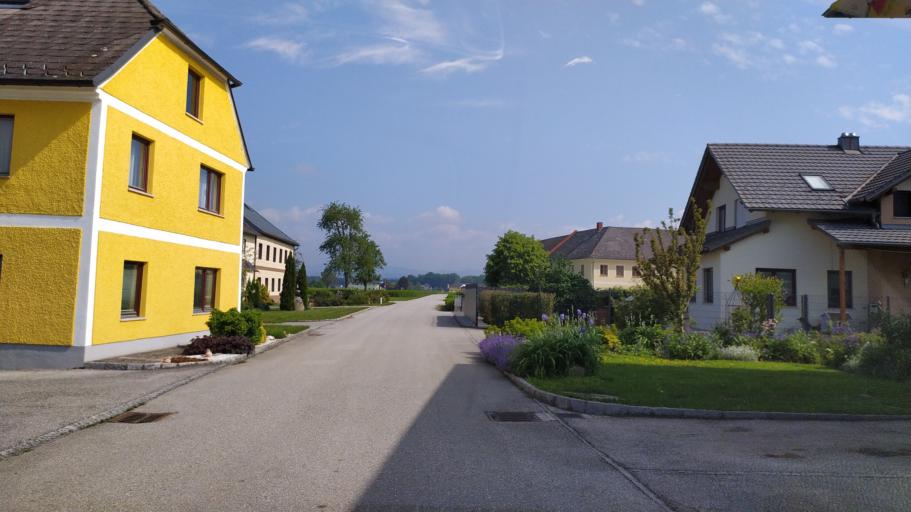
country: AT
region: Upper Austria
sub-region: Politischer Bezirk Perg
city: Perg
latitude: 48.1985
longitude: 14.6642
